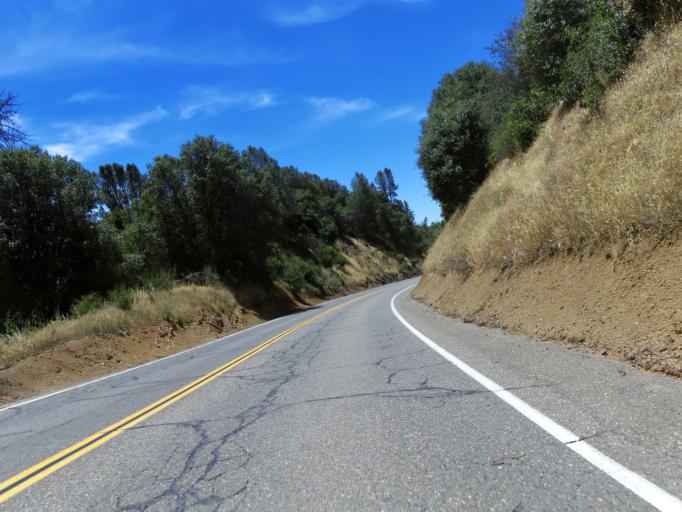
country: US
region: California
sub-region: Mariposa County
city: Mariposa
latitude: 37.5061
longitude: -119.9659
